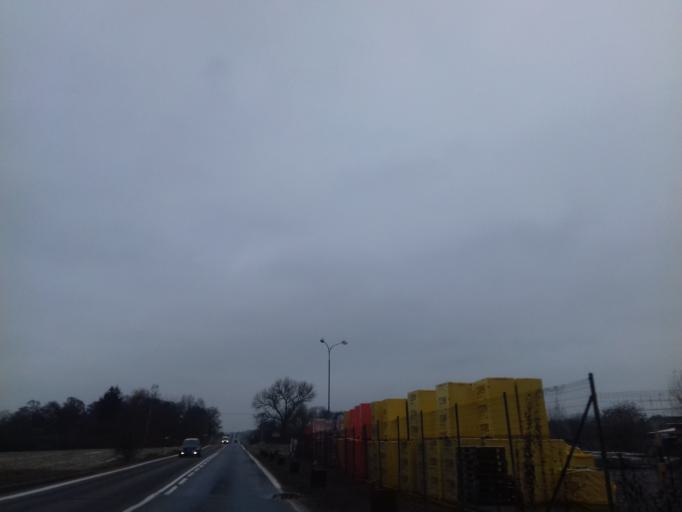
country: CZ
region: Plzensky
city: Holysov
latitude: 49.5923
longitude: 13.0928
